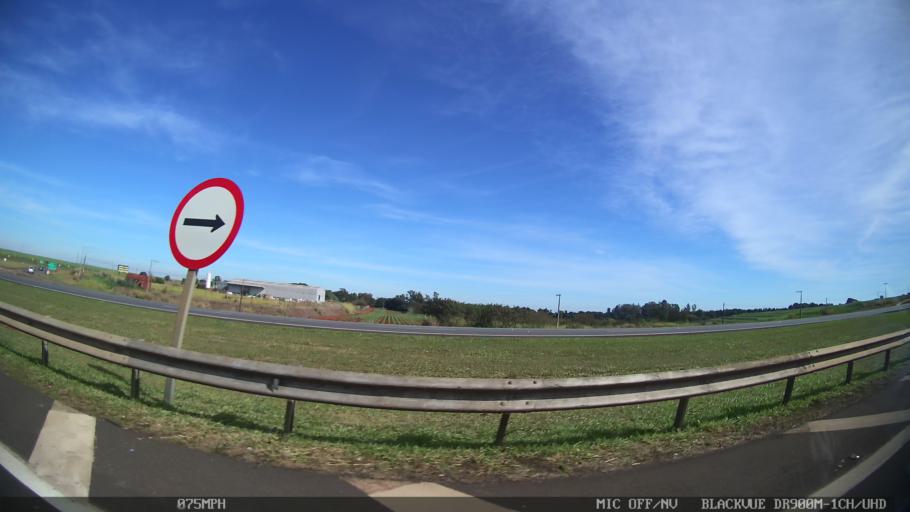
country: BR
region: Sao Paulo
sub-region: Cordeiropolis
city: Cordeiropolis
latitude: -22.4685
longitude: -47.3989
